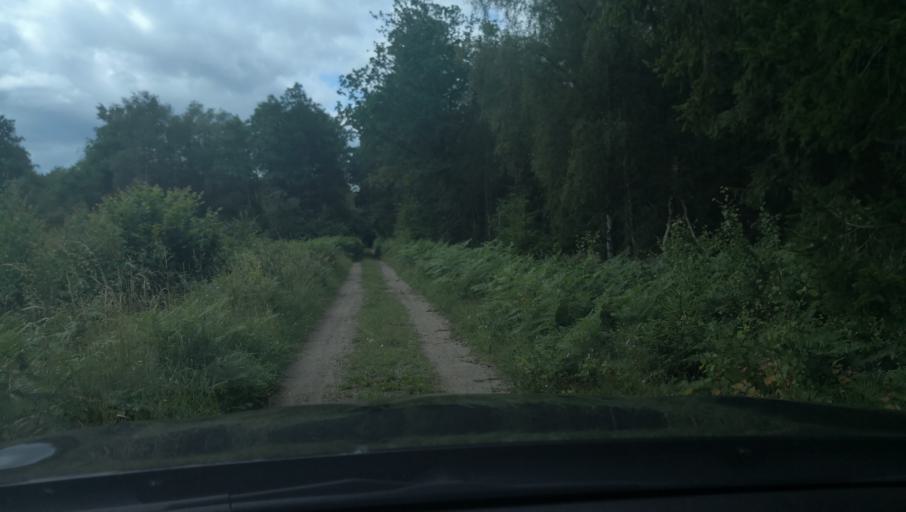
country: SE
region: Skane
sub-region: Simrishamns Kommun
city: Kivik
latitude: 55.6189
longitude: 14.1098
